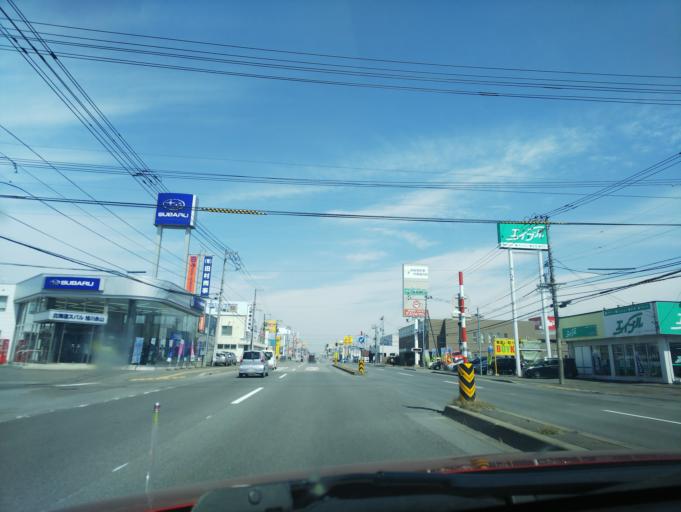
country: JP
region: Hokkaido
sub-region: Asahikawa-shi
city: Asahikawa
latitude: 43.7897
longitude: 142.4012
